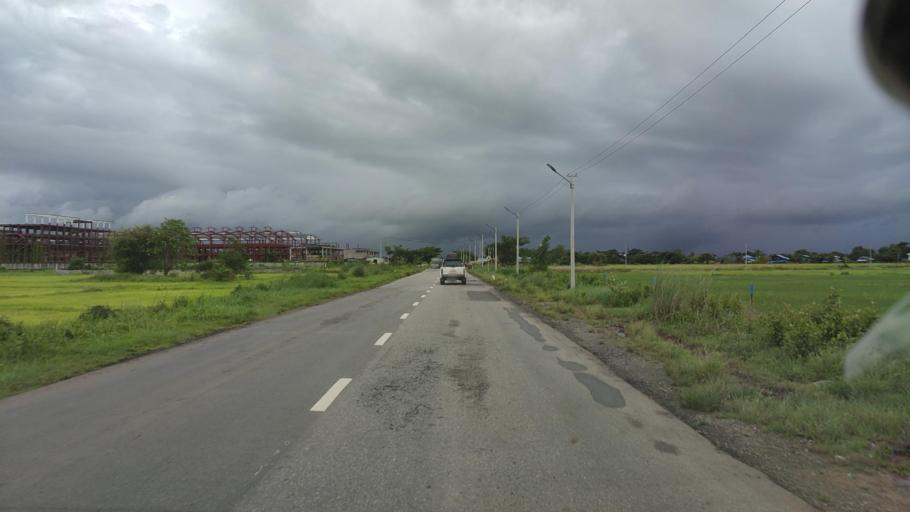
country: MM
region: Bago
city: Bago
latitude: 17.3876
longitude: 96.5057
